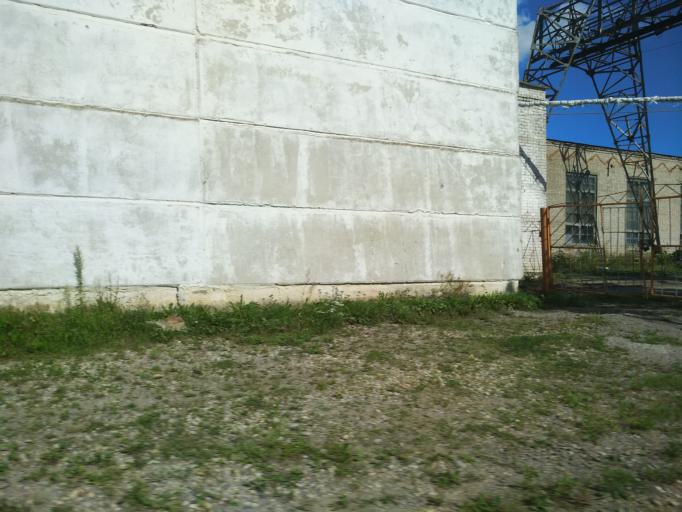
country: BY
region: Vitebsk
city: Mosar
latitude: 55.1245
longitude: 27.2110
